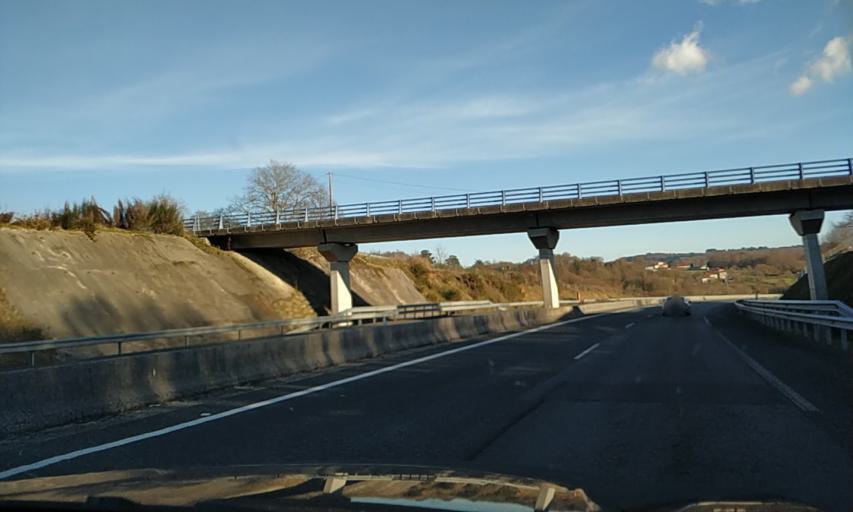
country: ES
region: Galicia
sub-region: Provincia de Pontevedra
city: Lalin
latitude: 42.6491
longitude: -8.1353
